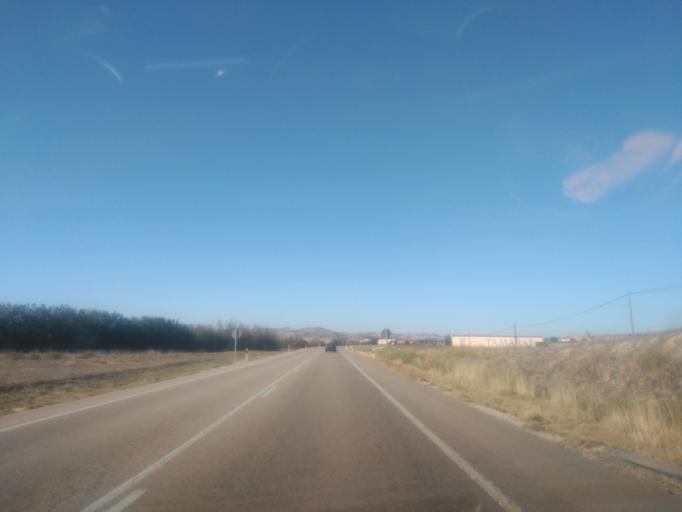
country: ES
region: Castille and Leon
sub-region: Provincia de Valladolid
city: Penafiel
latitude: 41.6081
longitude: -4.1457
